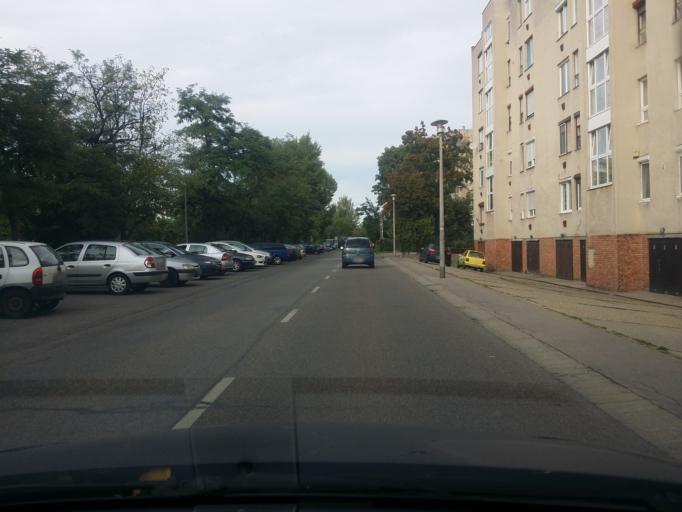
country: HU
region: Budapest
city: Budapest IV. keruelet
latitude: 47.5789
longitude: 19.0948
